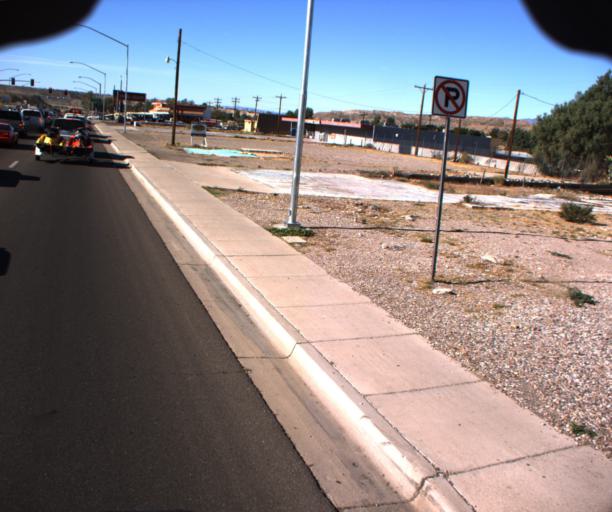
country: US
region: Arizona
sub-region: Mohave County
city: Bullhead City
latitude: 35.1473
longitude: -114.5685
